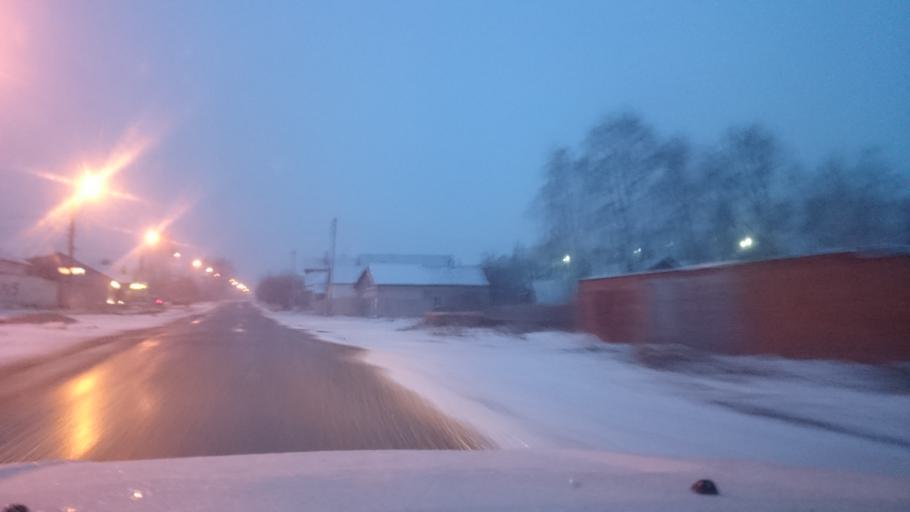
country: RU
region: Tula
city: Barsuki
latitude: 54.2029
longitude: 37.5366
